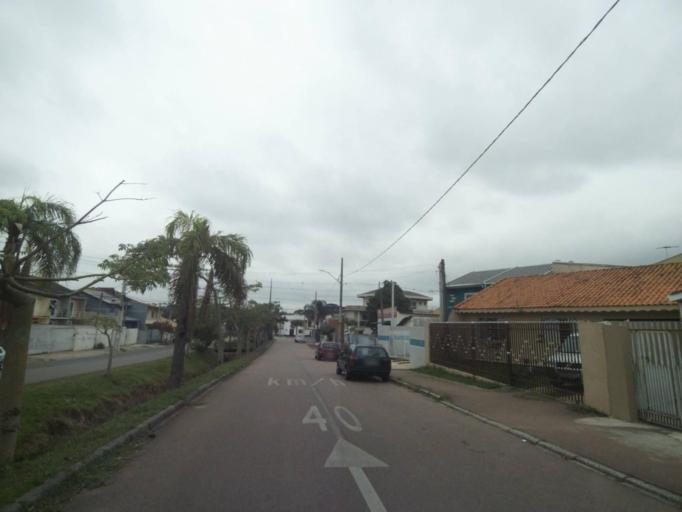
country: BR
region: Parana
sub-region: Araucaria
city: Araucaria
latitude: -25.5408
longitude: -49.3372
